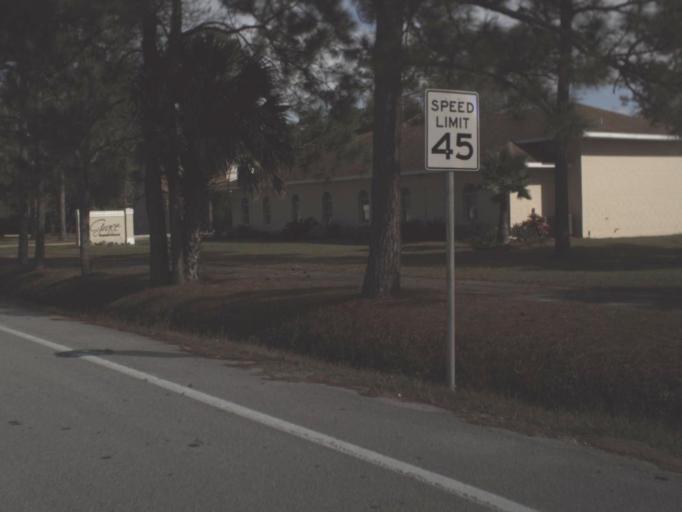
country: US
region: Florida
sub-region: Volusia County
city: Samsula-Spruce Creek
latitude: 29.1011
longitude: -81.0404
